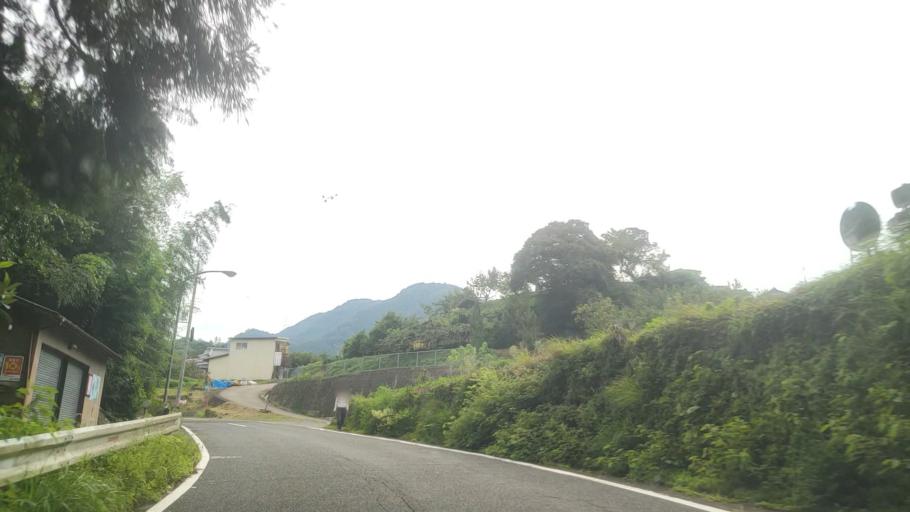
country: JP
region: Wakayama
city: Koya
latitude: 34.2602
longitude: 135.5467
